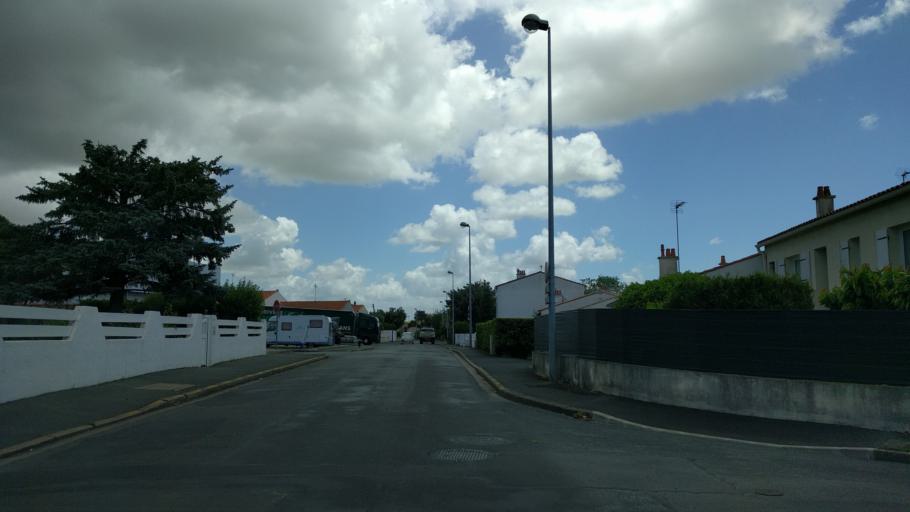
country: FR
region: Poitou-Charentes
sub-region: Departement de la Charente-Maritime
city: Puilboreau
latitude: 46.1678
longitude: -1.1274
